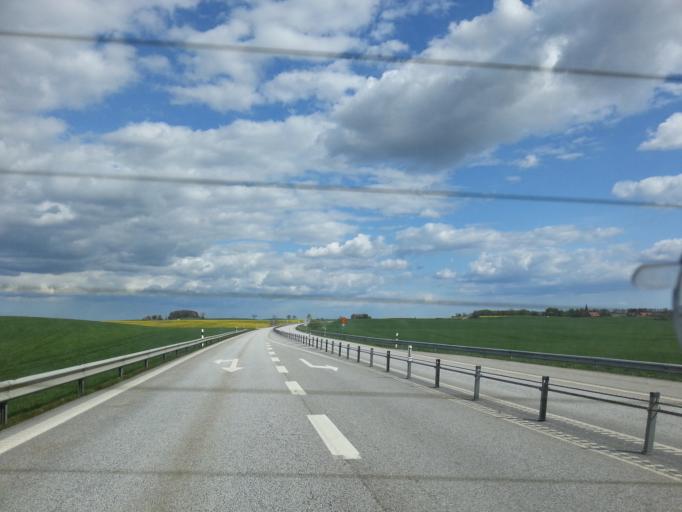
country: SE
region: Skane
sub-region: Skurups Kommun
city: Rydsgard
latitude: 55.4721
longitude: 13.6910
